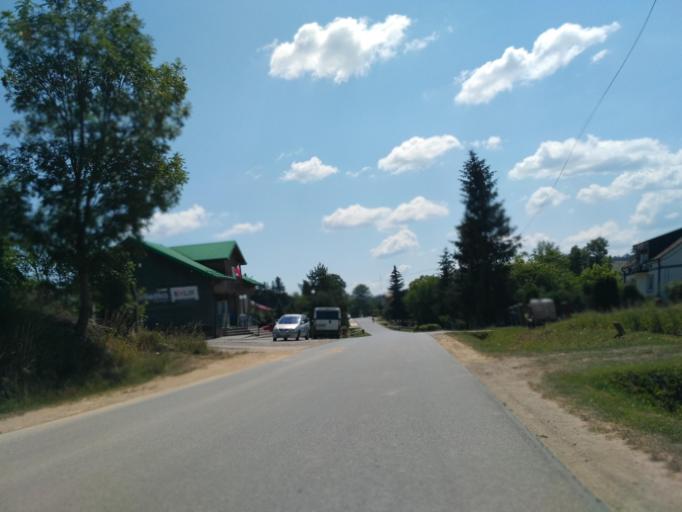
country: PL
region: Subcarpathian Voivodeship
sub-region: Powiat sanocki
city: Niebieszczany
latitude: 49.5000
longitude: 22.1625
